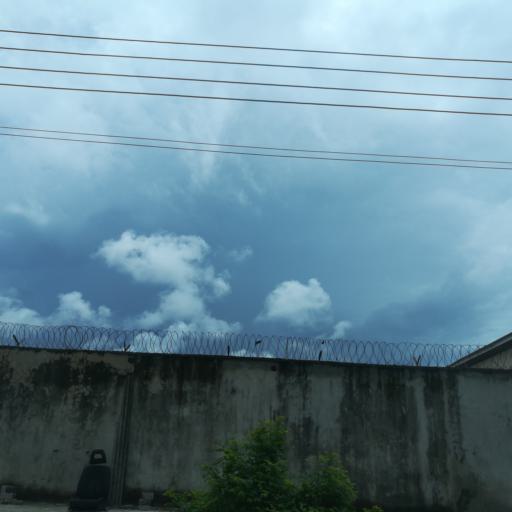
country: NG
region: Lagos
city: Ikoyi
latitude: 6.4458
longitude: 3.4624
